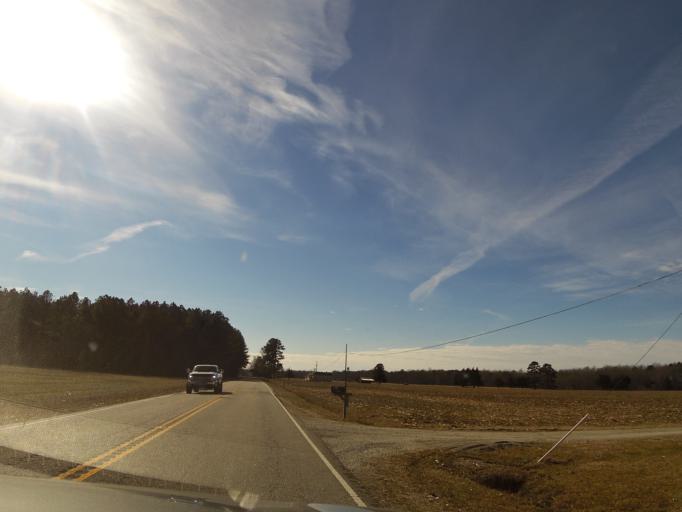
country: US
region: Virginia
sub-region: Isle of Wight County
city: Isle of Wight
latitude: 36.9210
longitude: -76.6922
